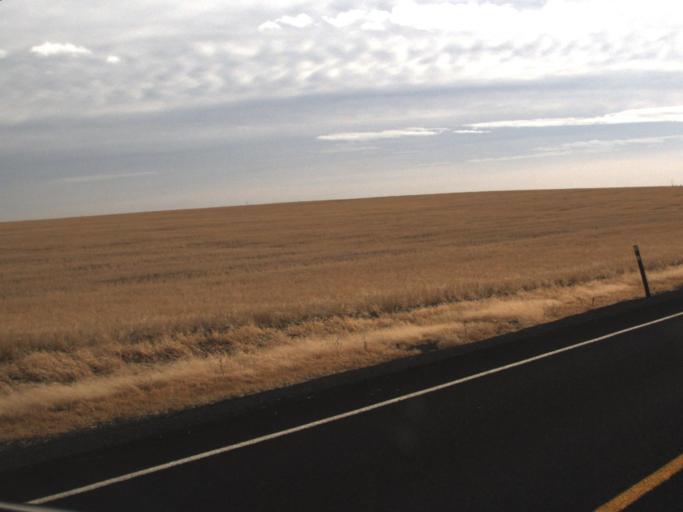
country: US
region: Washington
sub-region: Okanogan County
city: Coulee Dam
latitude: 47.7832
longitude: -118.7219
